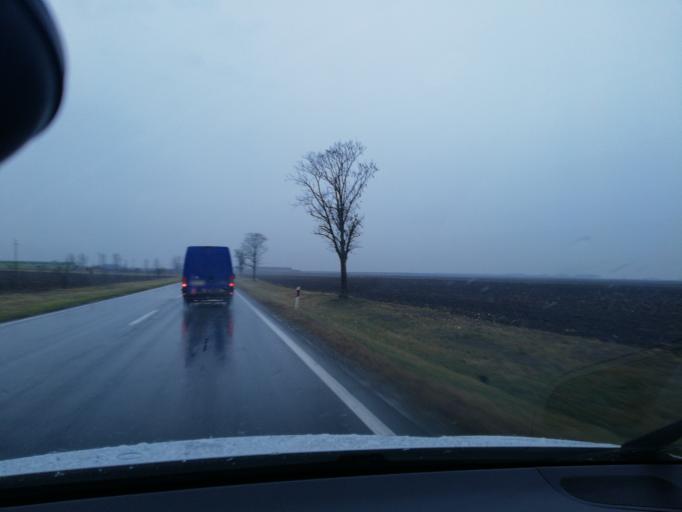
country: RS
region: Autonomna Pokrajina Vojvodina
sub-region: Sremski Okrug
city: Ruma
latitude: 45.0477
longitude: 19.8420
